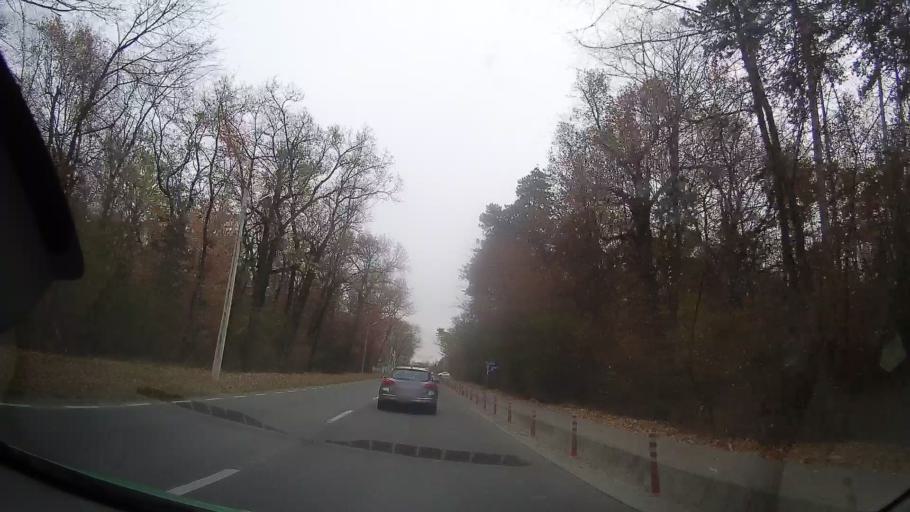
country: RO
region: Prahova
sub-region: Comuna Paulesti
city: Gageni
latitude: 45.0100
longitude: 25.9536
